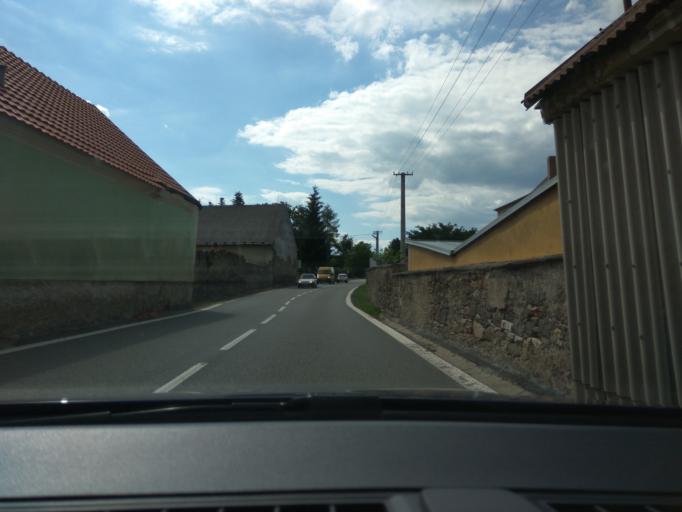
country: CZ
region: Jihocesky
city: Kovarov
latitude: 49.4743
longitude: 14.2882
